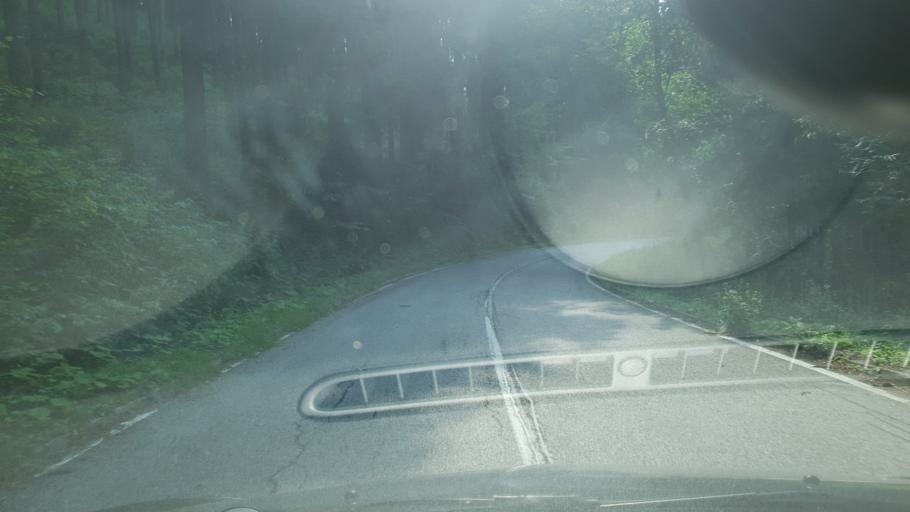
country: HR
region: Grad Zagreb
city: Kasina
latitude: 45.9186
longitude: 15.9804
